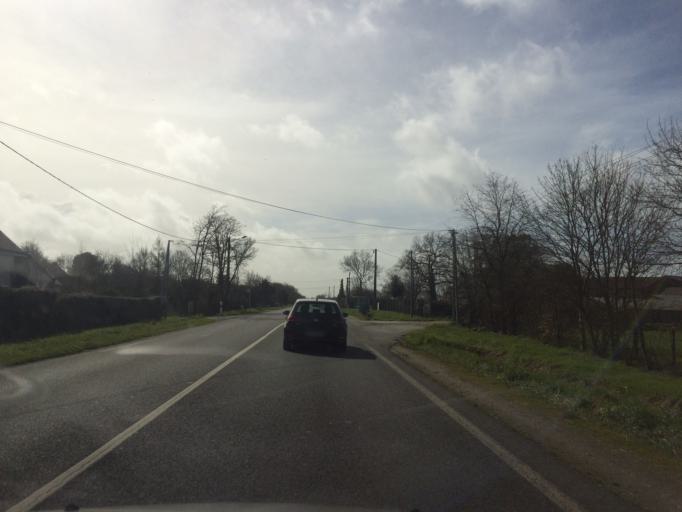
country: FR
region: Pays de la Loire
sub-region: Departement de la Loire-Atlantique
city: Besne
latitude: 47.3770
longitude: -2.0974
